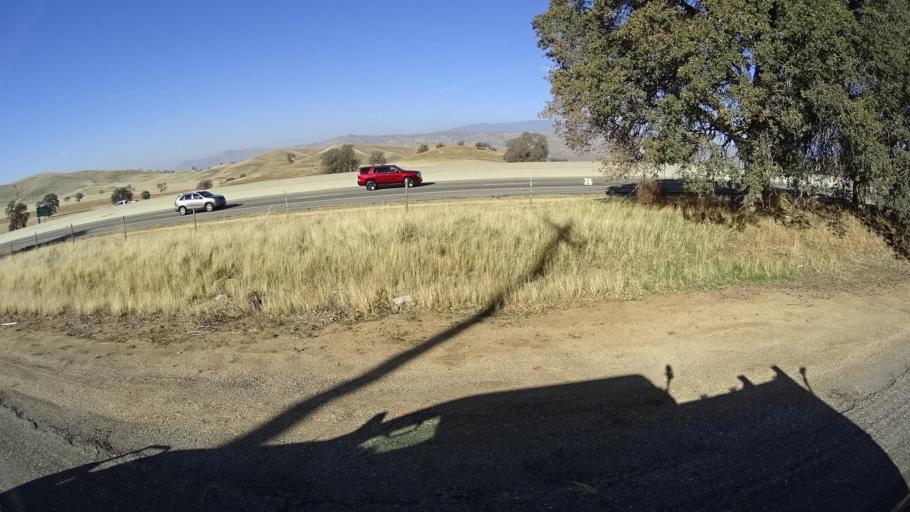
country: US
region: California
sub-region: Kern County
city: Bear Valley Springs
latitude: 35.2635
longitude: -118.6525
